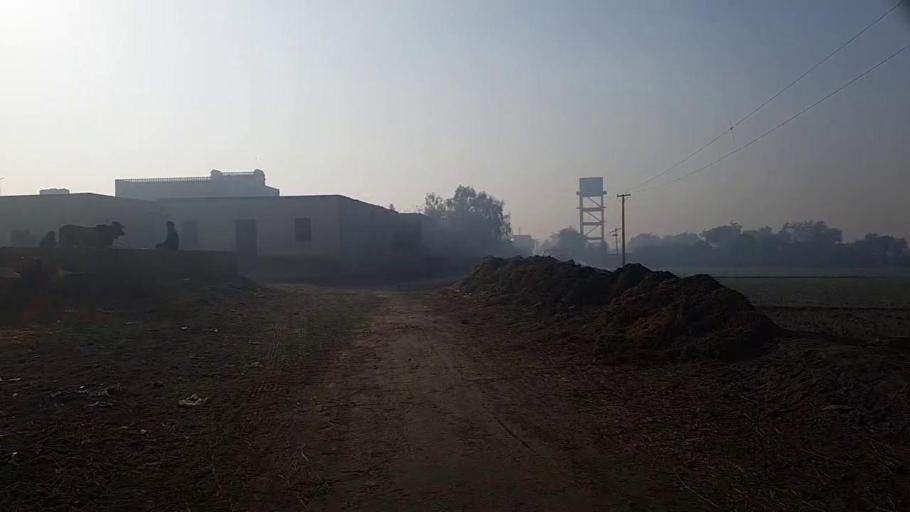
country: PK
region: Sindh
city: Mehar
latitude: 27.1360
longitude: 67.8232
